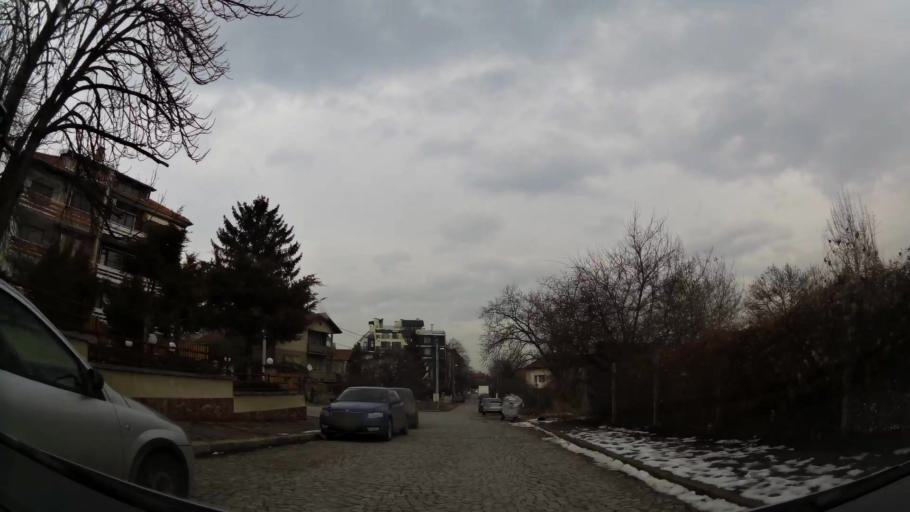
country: BG
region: Sofia-Capital
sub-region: Stolichna Obshtina
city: Sofia
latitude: 42.6627
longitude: 23.2422
